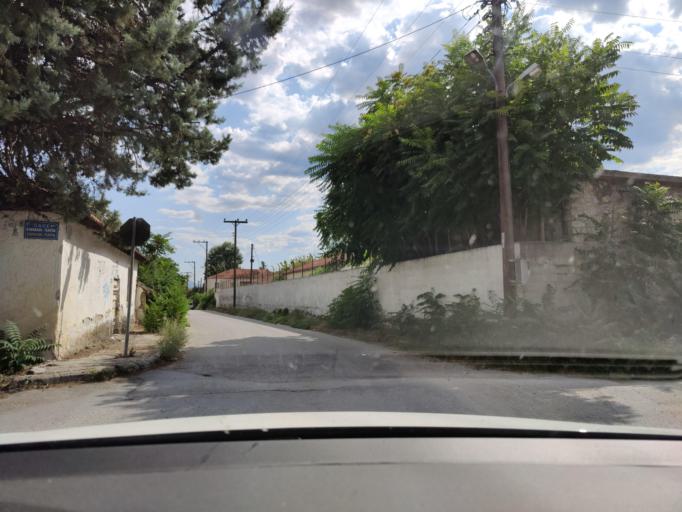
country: GR
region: Central Macedonia
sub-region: Nomos Serron
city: Serres
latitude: 41.0881
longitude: 23.5323
